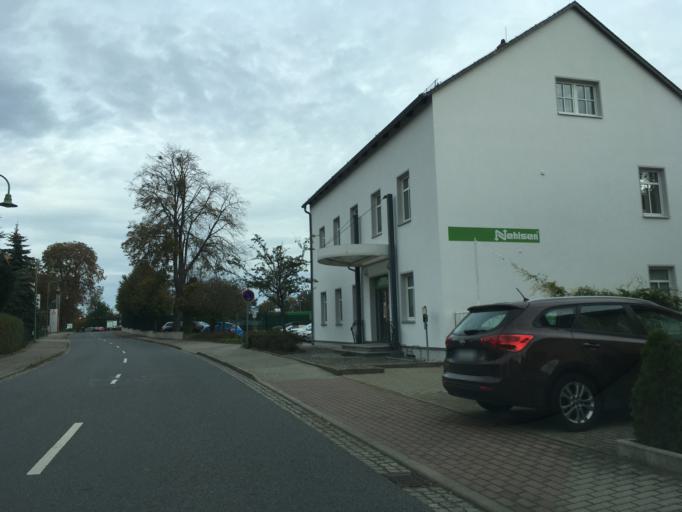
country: DE
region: Saxony
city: Radeberg
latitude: 51.1077
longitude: 13.9219
